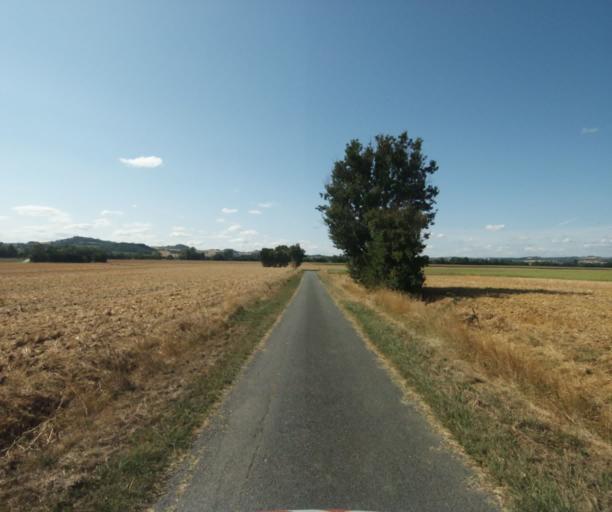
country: FR
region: Midi-Pyrenees
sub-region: Departement de la Haute-Garonne
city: Revel
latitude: 43.5052
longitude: 1.9735
